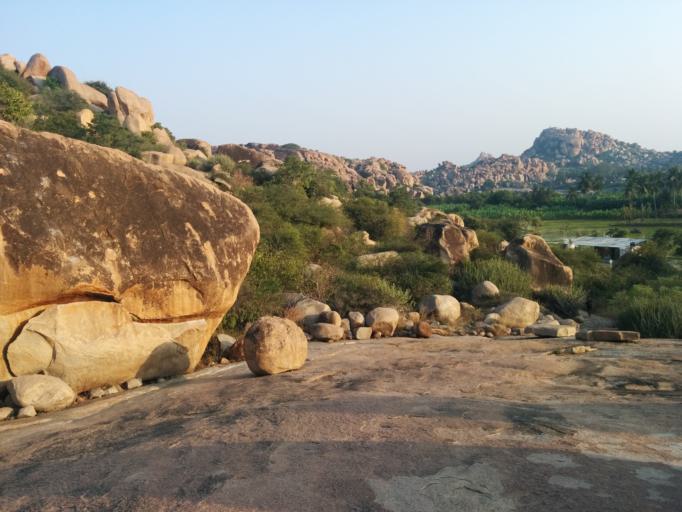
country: IN
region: Karnataka
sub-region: Bellary
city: Hampi
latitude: 15.3419
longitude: 76.4628
